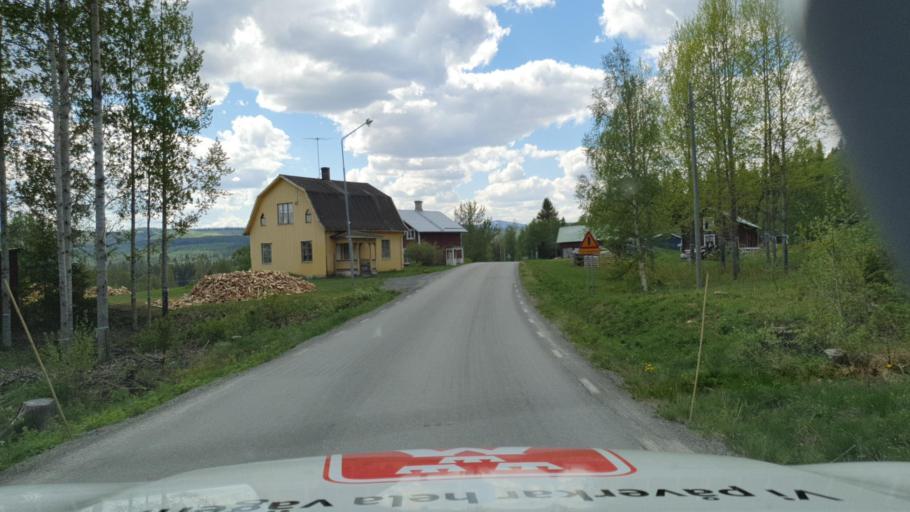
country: SE
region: Jaemtland
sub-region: Krokoms Kommun
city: Valla
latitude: 63.9693
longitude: 14.1439
